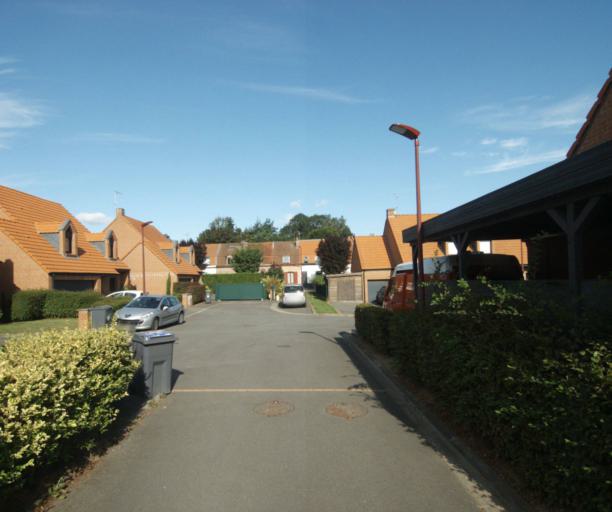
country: FR
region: Nord-Pas-de-Calais
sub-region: Departement du Nord
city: Sainghin-en-Melantois
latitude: 50.5824
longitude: 3.1715
